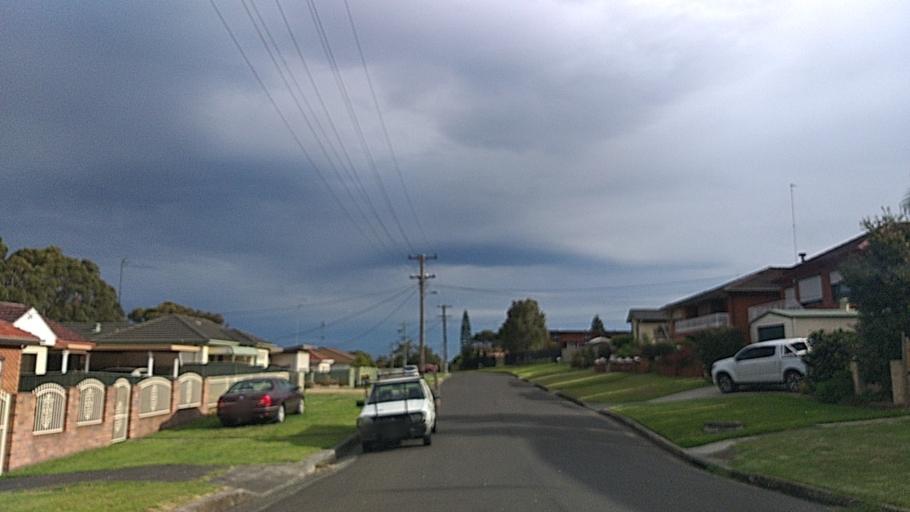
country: AU
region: New South Wales
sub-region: Wollongong
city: Lake Heights
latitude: -34.4897
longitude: 150.8729
